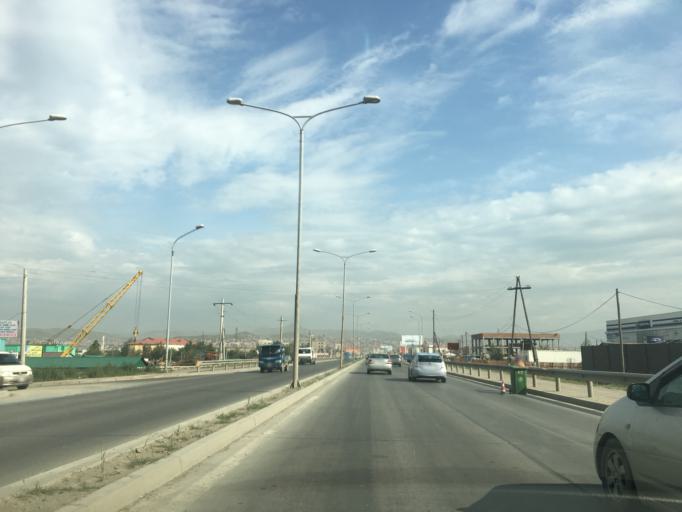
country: MN
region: Ulaanbaatar
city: Ulaanbaatar
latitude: 47.8970
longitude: 106.7856
